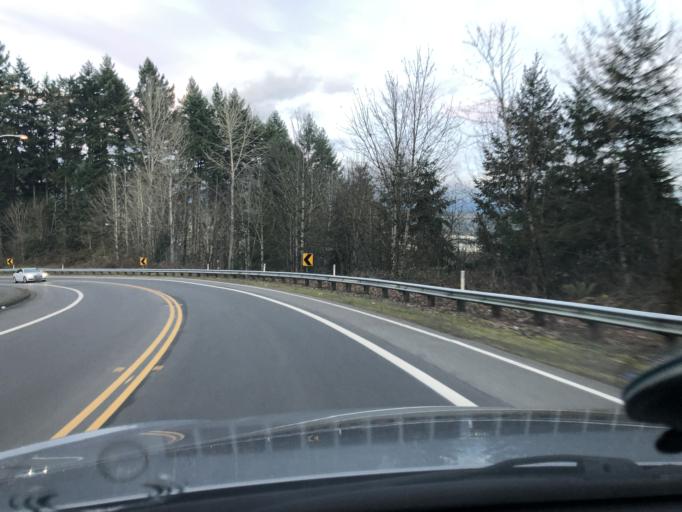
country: US
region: Washington
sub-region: King County
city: Lakeland North
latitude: 47.3158
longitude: -122.2565
